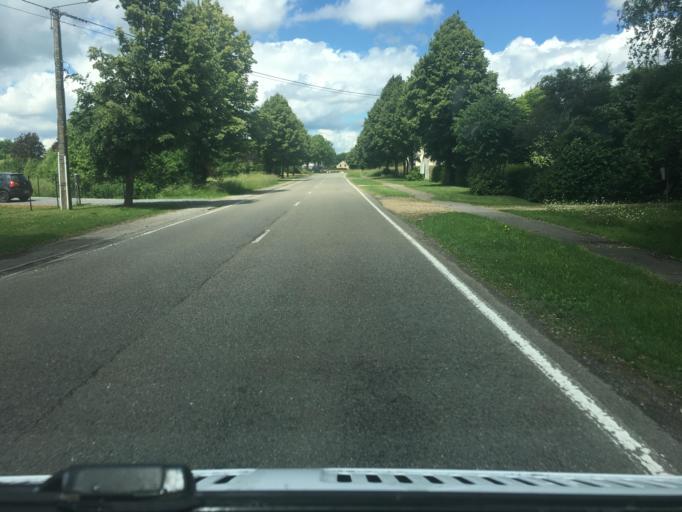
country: BE
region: Wallonia
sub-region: Province du Luxembourg
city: Florenville
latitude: 49.6835
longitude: 5.3318
